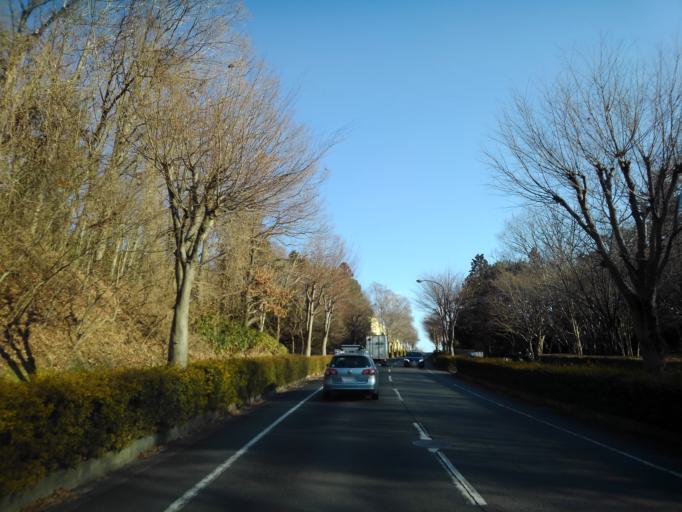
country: JP
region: Saitama
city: Hanno
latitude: 35.8393
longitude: 139.3090
